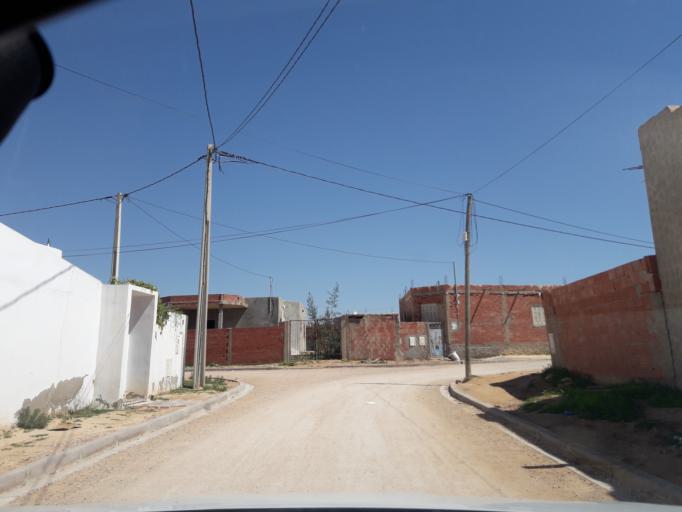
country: TN
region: Safaqis
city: Sfax
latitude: 34.7430
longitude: 10.5181
